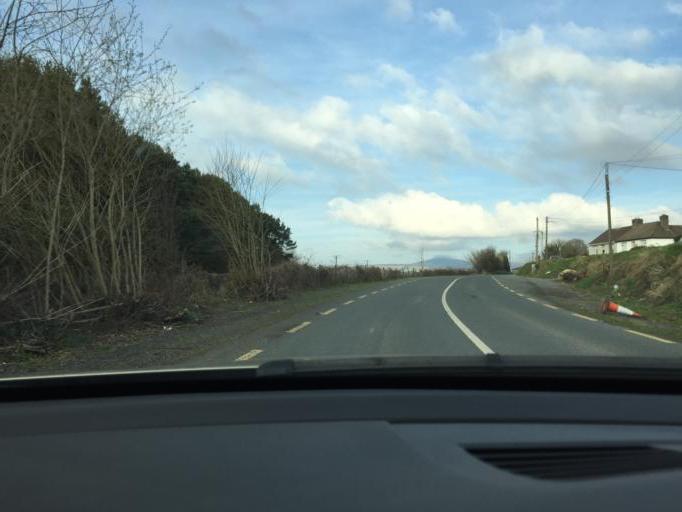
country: IE
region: Leinster
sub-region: Wicklow
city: Blessington
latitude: 53.1683
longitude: -6.5213
